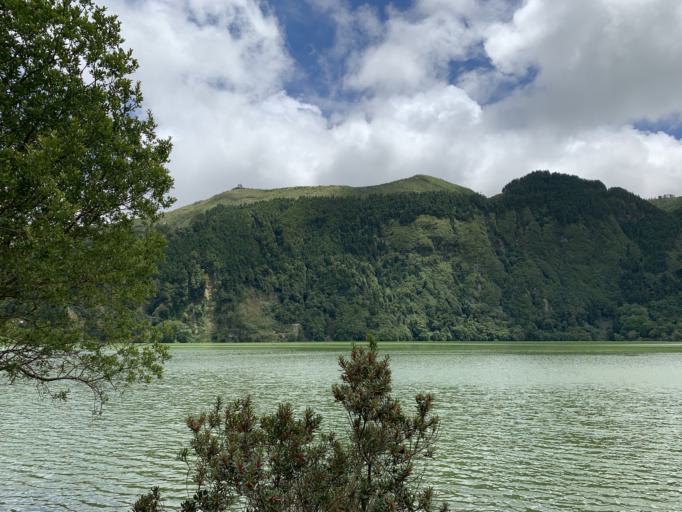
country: PT
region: Azores
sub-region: Ponta Delgada
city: Arrifes
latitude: 37.8493
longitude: -25.7920
